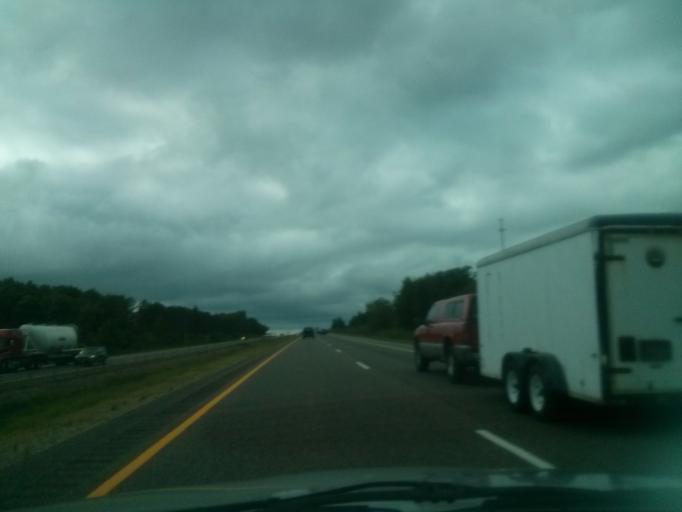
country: US
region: Wisconsin
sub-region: Saint Croix County
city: Baldwin
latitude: 44.9403
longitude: -92.4101
